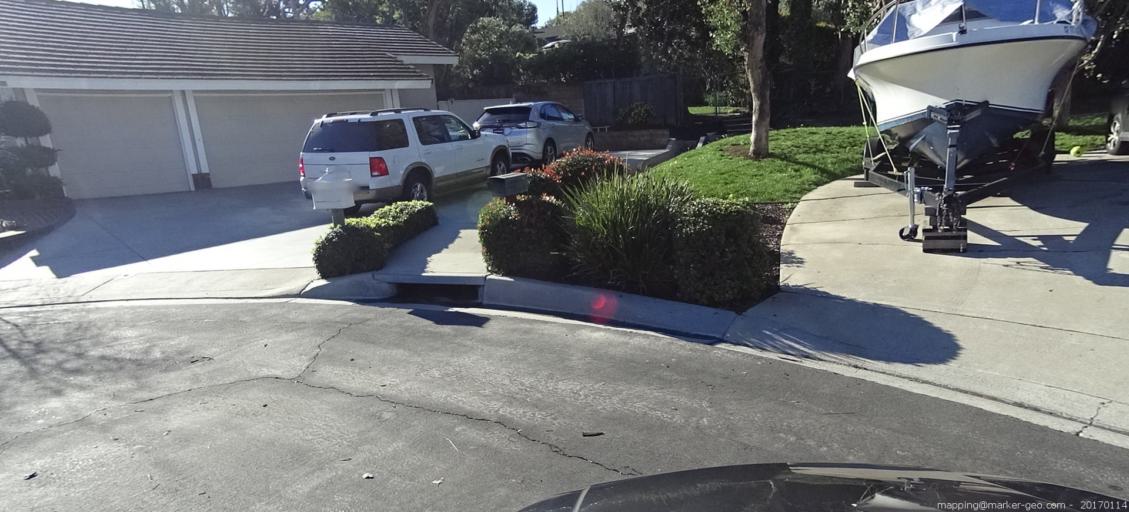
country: US
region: California
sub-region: Orange County
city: North Tustin
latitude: 33.7775
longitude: -117.7919
